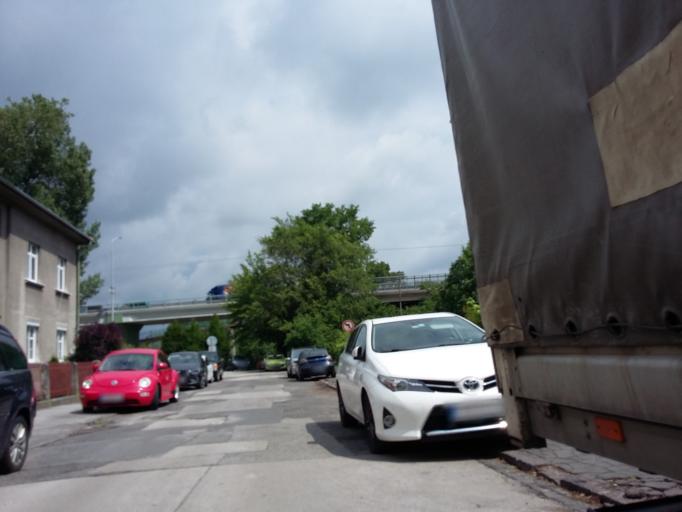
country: SK
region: Bratislavsky
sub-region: Okres Malacky
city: Malacky
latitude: 48.4371
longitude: 17.0234
